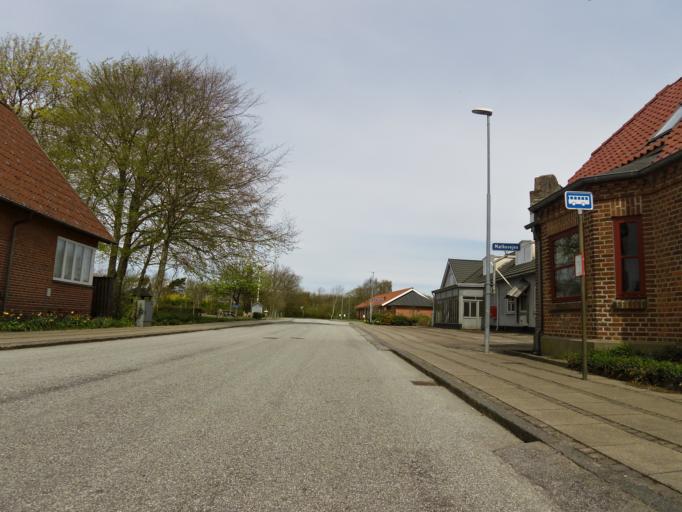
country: DK
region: Central Jutland
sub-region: Skive Kommune
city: Skive
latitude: 56.5341
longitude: 8.9323
